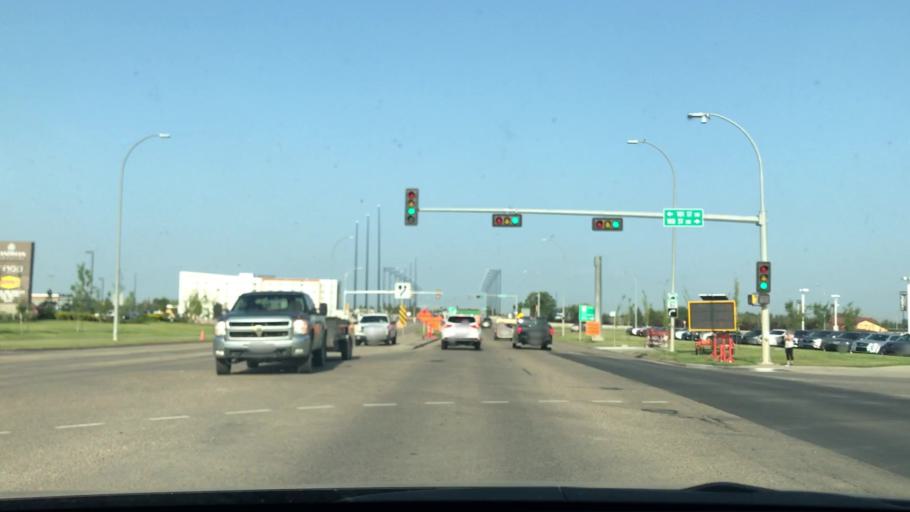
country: CA
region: Alberta
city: Beaumont
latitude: 53.4249
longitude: -113.4890
